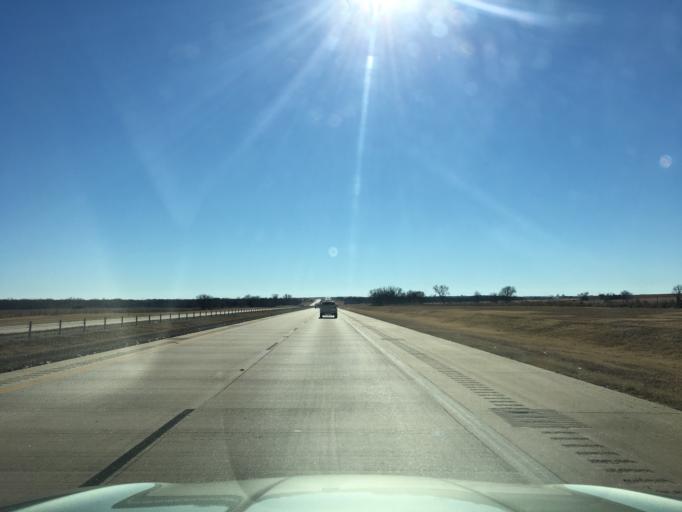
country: US
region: Oklahoma
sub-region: Noble County
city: Perry
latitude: 36.4462
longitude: -97.3271
